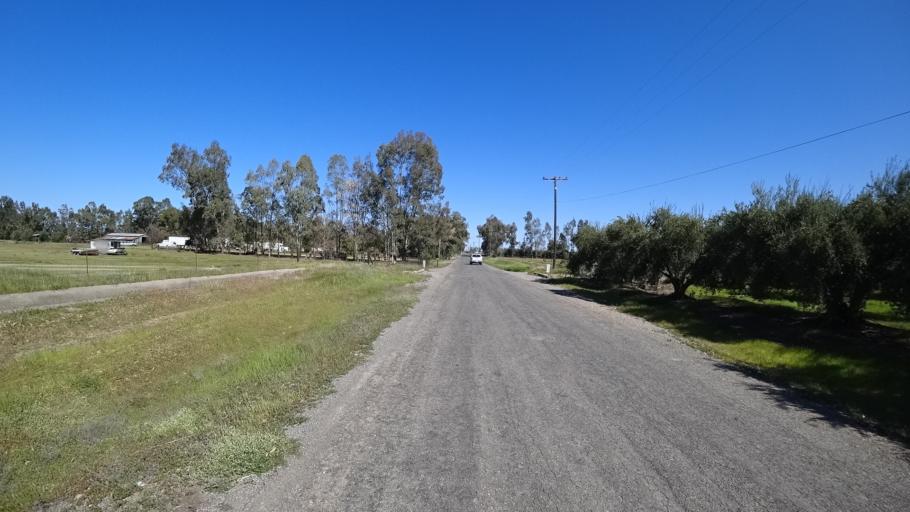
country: US
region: California
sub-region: Glenn County
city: Orland
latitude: 39.7161
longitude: -122.2113
